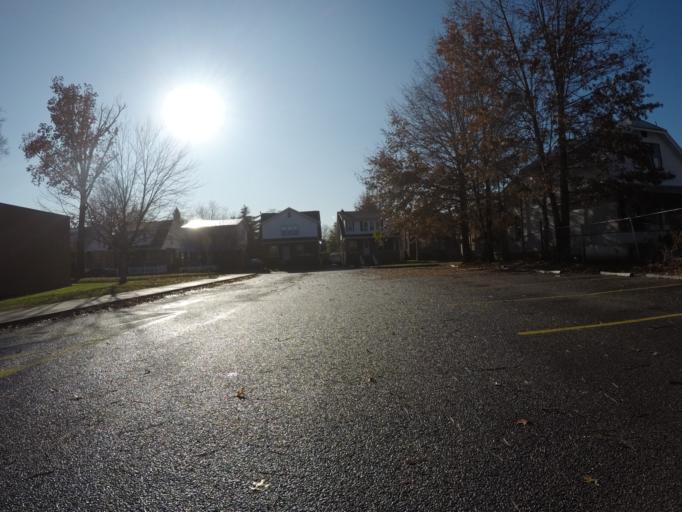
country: US
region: Ohio
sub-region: Lawrence County
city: Burlington
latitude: 38.4104
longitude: -82.4913
